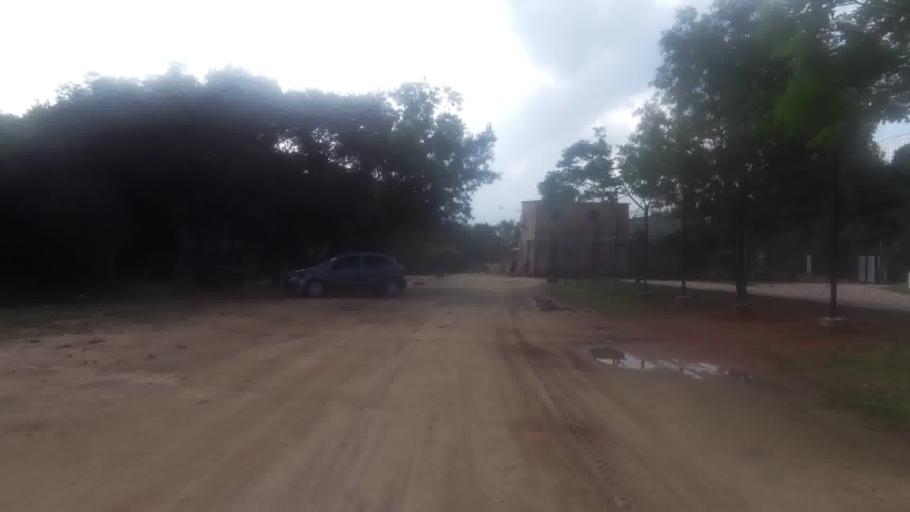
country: BR
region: Espirito Santo
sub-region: Guarapari
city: Guarapari
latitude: -20.7696
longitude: -40.5763
